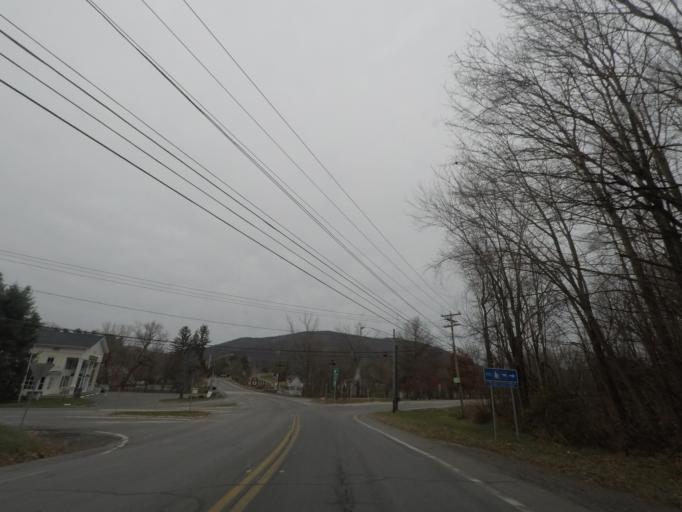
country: US
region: Massachusetts
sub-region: Berkshire County
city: Williamstown
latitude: 42.6611
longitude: -73.2415
